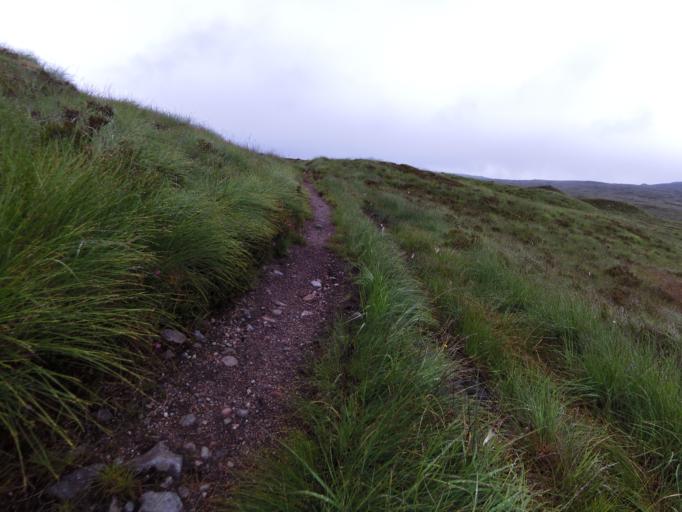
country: GB
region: Scotland
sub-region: Highland
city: Spean Bridge
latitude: 56.7657
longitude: -4.7015
